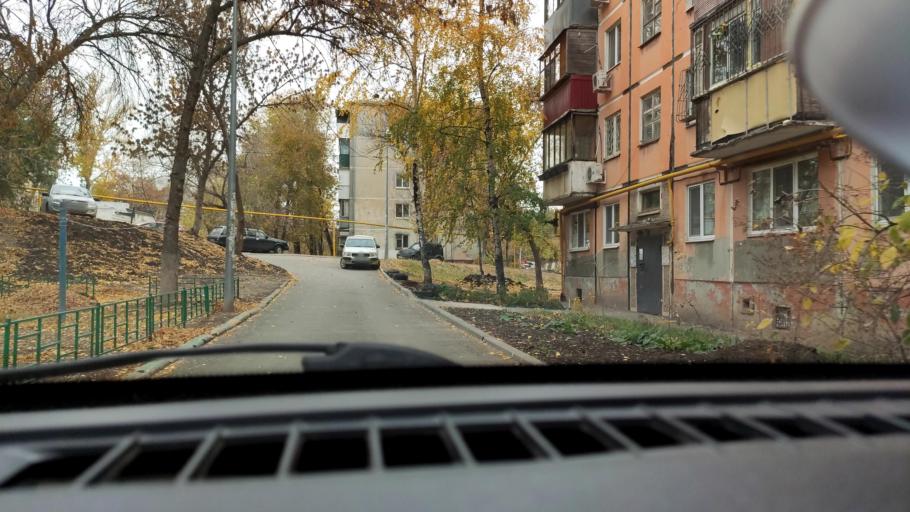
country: RU
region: Samara
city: Samara
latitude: 53.1904
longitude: 50.1940
